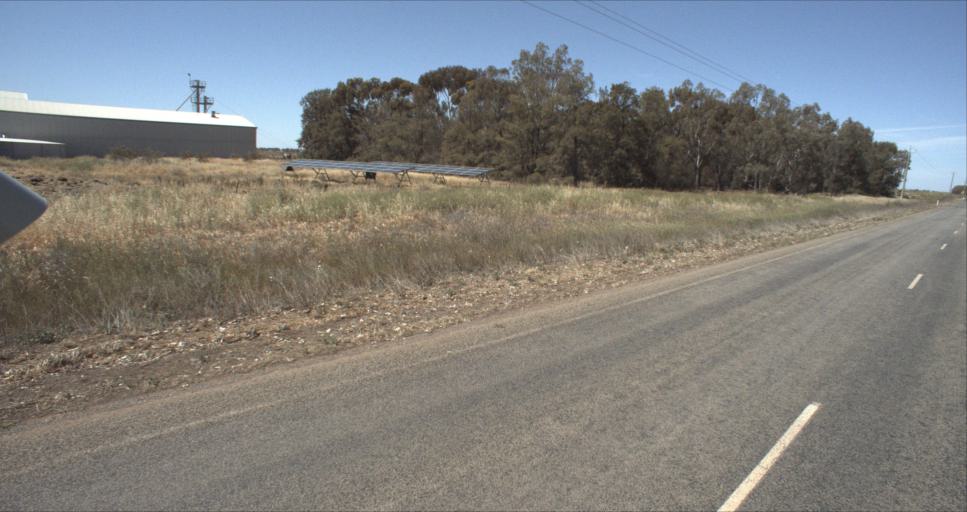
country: AU
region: New South Wales
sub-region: Leeton
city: Leeton
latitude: -34.4692
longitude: 146.2927
